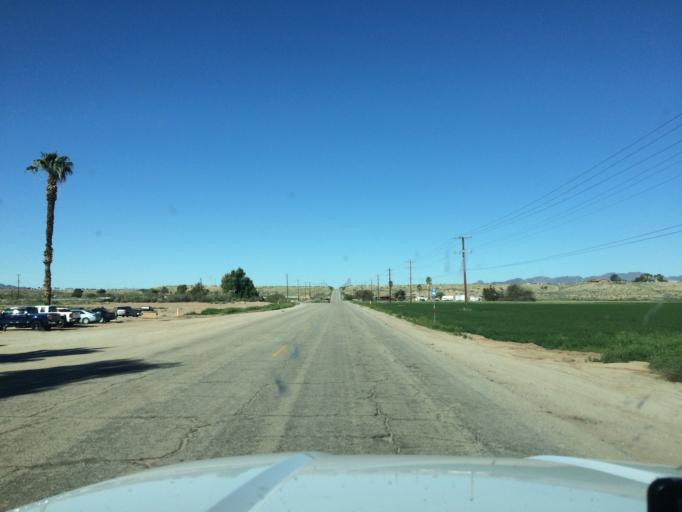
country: US
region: California
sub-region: Riverside County
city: Blythe
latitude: 33.6102
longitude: -114.6587
